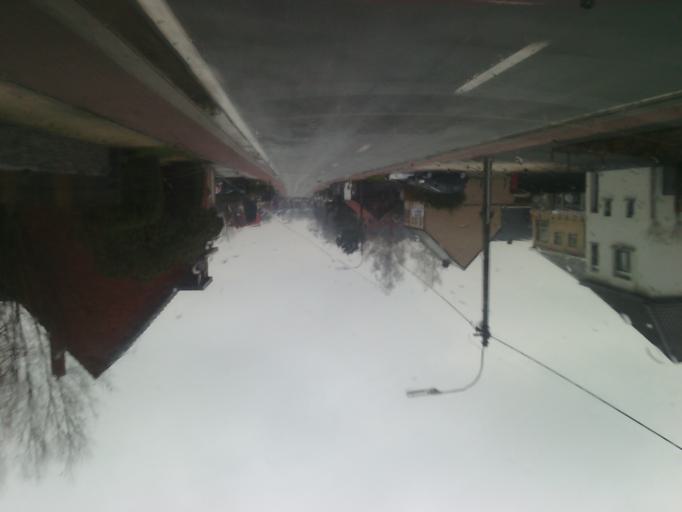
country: BE
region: Flanders
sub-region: Provincie Oost-Vlaanderen
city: Wetteren
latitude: 51.0111
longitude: 3.9104
